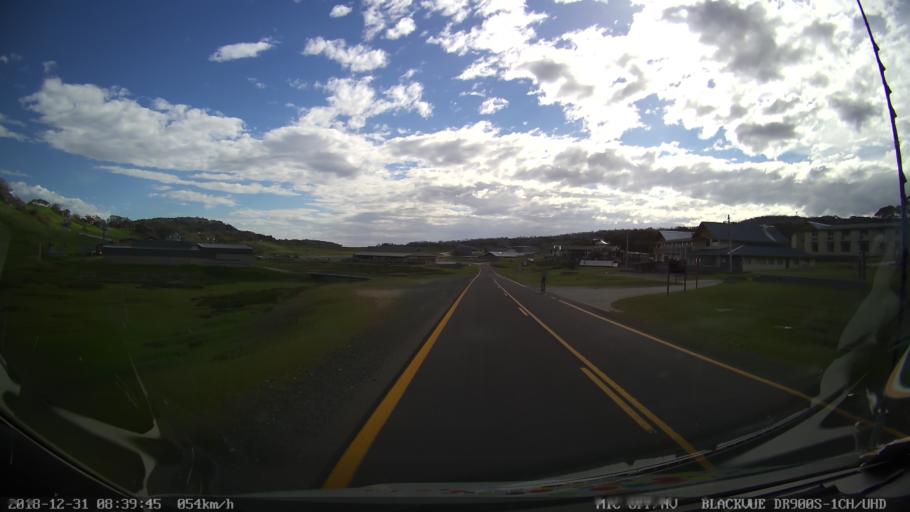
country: AU
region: New South Wales
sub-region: Snowy River
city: Jindabyne
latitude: -36.4072
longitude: 148.4085
